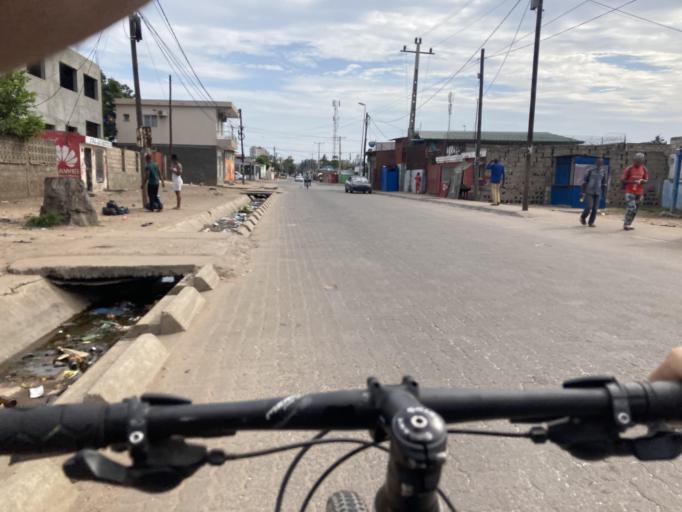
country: MZ
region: Maputo City
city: Maputo
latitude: -25.9478
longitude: 32.5819
